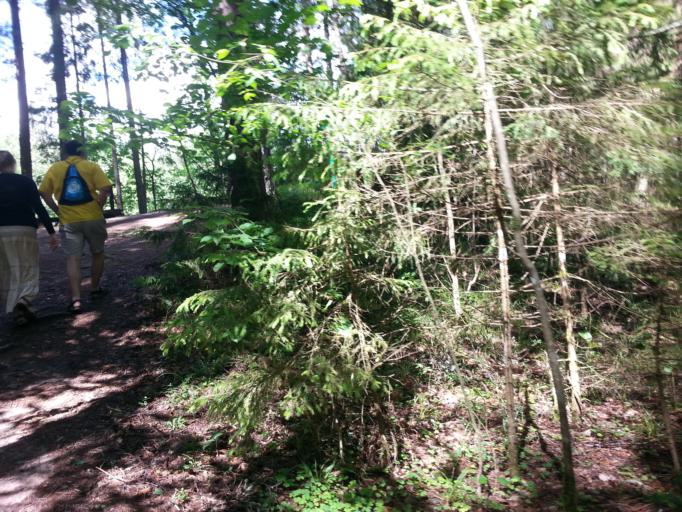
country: BY
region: Vitebsk
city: Lyntupy
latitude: 54.9658
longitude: 26.3714
